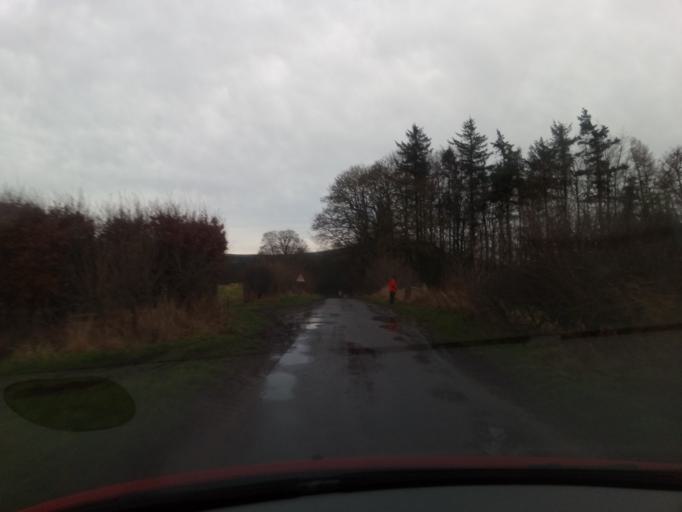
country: GB
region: England
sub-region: Northumberland
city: Wooler
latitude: 55.4959
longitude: -1.9136
